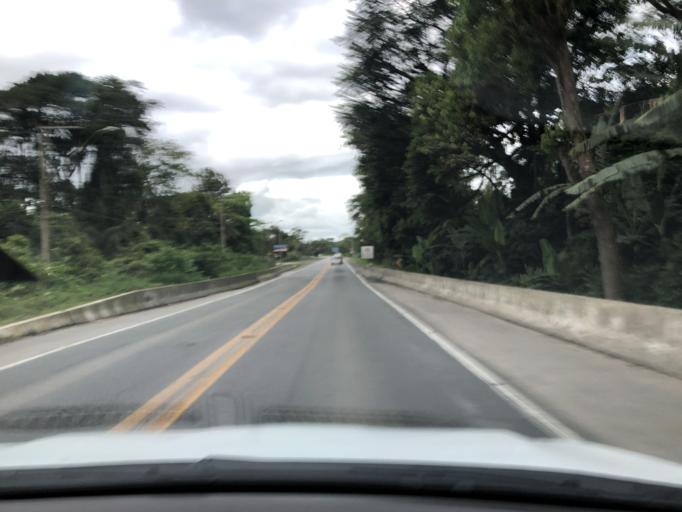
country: BR
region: Santa Catarina
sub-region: Sao Francisco Do Sul
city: Sao Francisco do Sul
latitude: -26.3060
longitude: -48.6415
